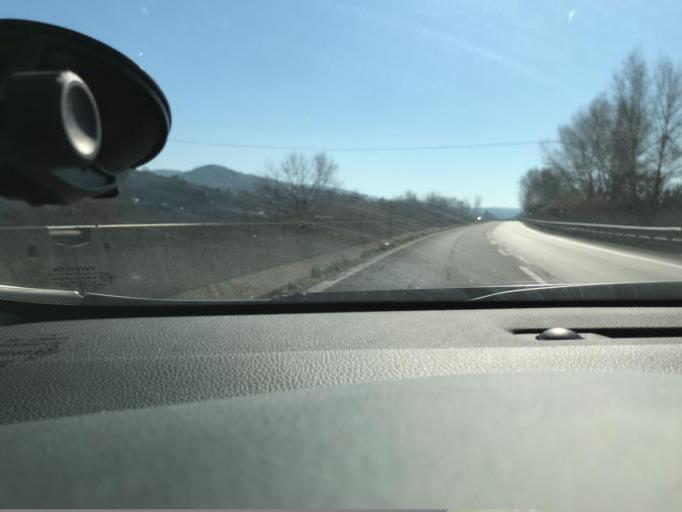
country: IT
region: Umbria
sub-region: Provincia di Perugia
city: Torgiano
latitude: 43.0123
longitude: 12.4258
